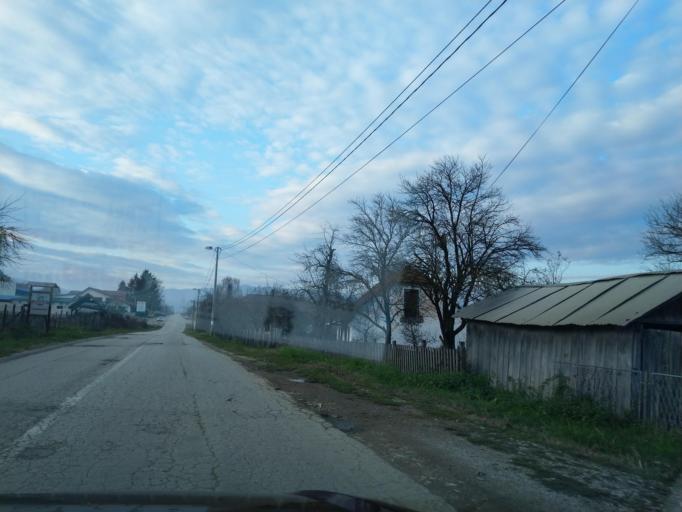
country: RS
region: Central Serbia
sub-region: Zlatiborski Okrug
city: Kosjeric
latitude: 43.9172
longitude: 19.9102
